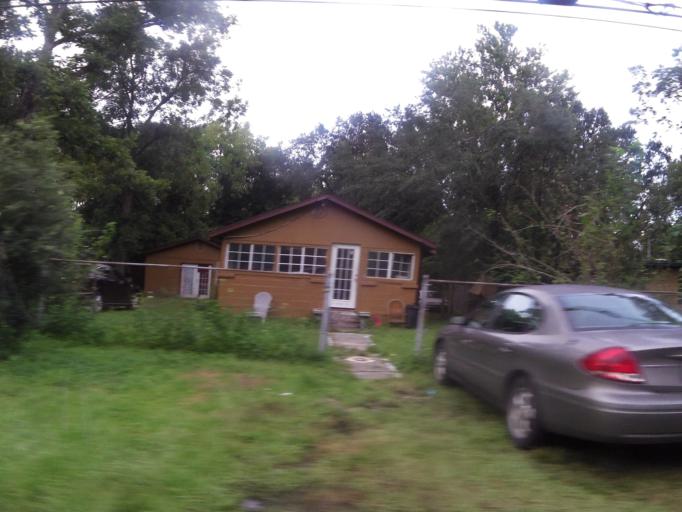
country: US
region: Florida
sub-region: Duval County
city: Jacksonville
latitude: 30.3439
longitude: -81.7176
